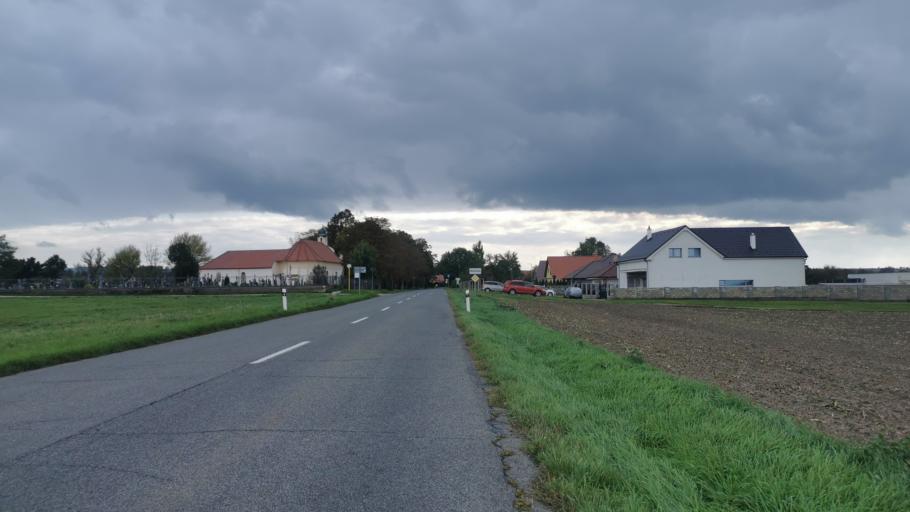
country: SK
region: Trnavsky
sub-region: Okres Skalica
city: Holic
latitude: 48.8107
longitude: 17.1946
